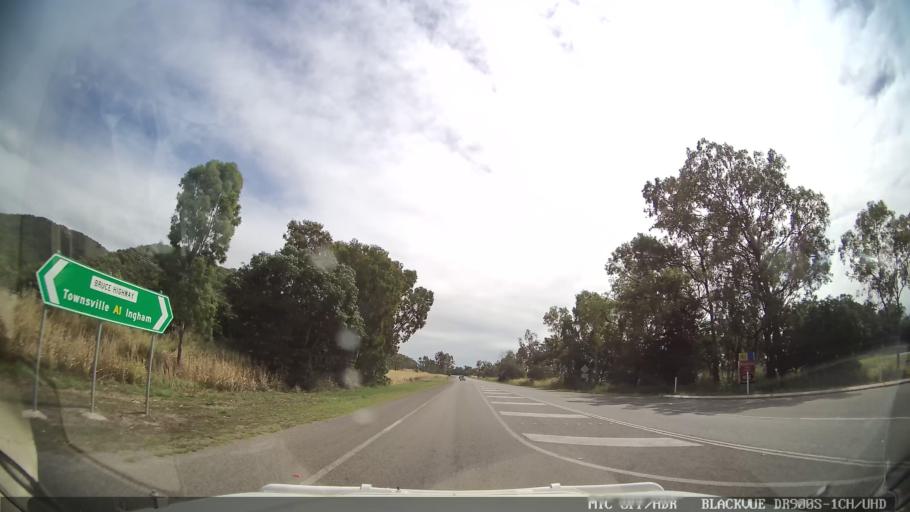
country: AU
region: Queensland
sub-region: Hinchinbrook
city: Ingham
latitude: -19.0158
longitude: 146.3662
